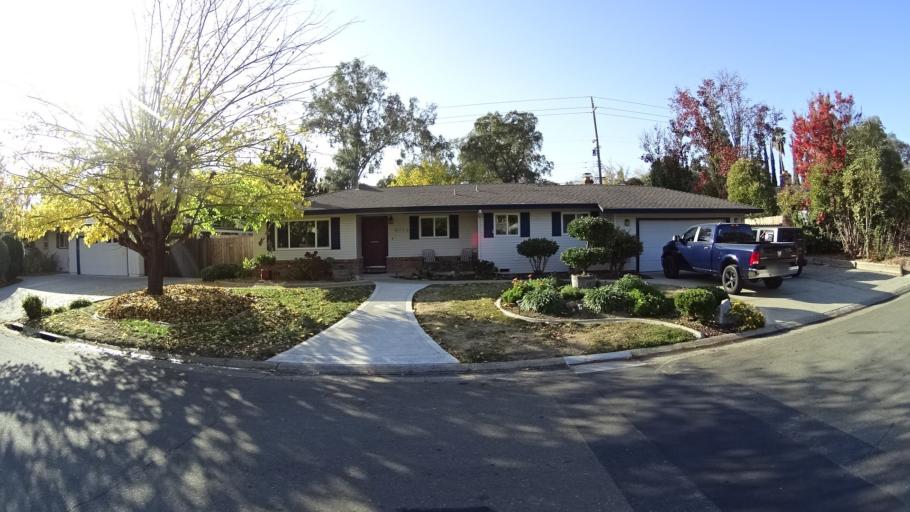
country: US
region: California
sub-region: Sacramento County
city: Fair Oaks
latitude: 38.6703
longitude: -121.2880
